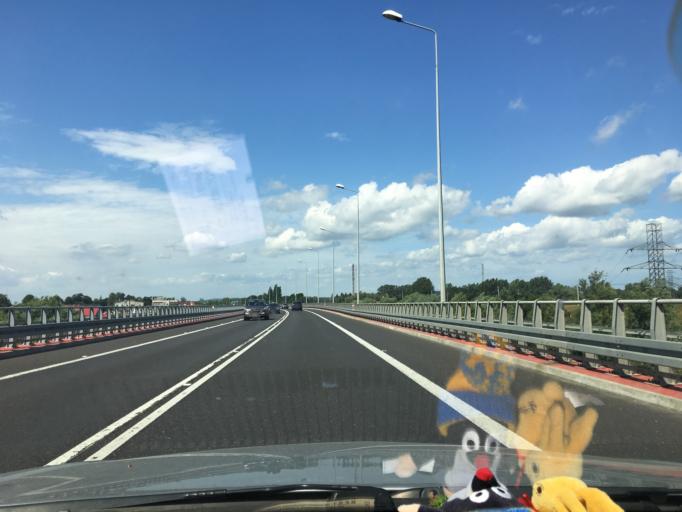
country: PL
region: West Pomeranian Voivodeship
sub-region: Powiat kamienski
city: Wolin
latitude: 53.8468
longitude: 14.6204
